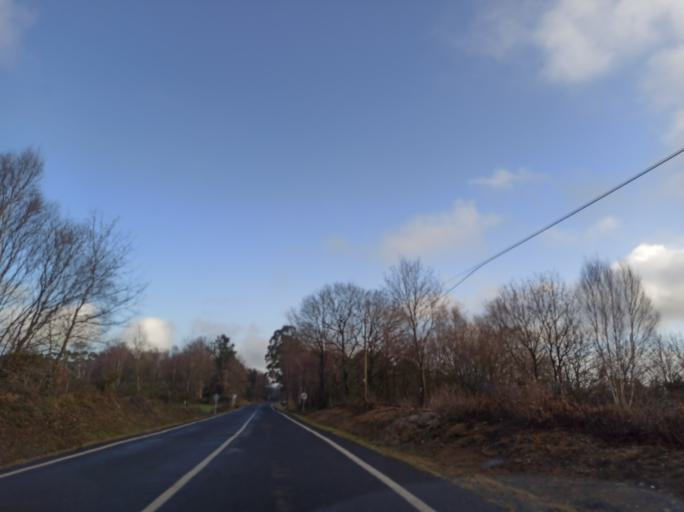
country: ES
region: Galicia
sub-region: Provincia da Coruna
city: Sobrado
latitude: 43.0866
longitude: -7.9989
